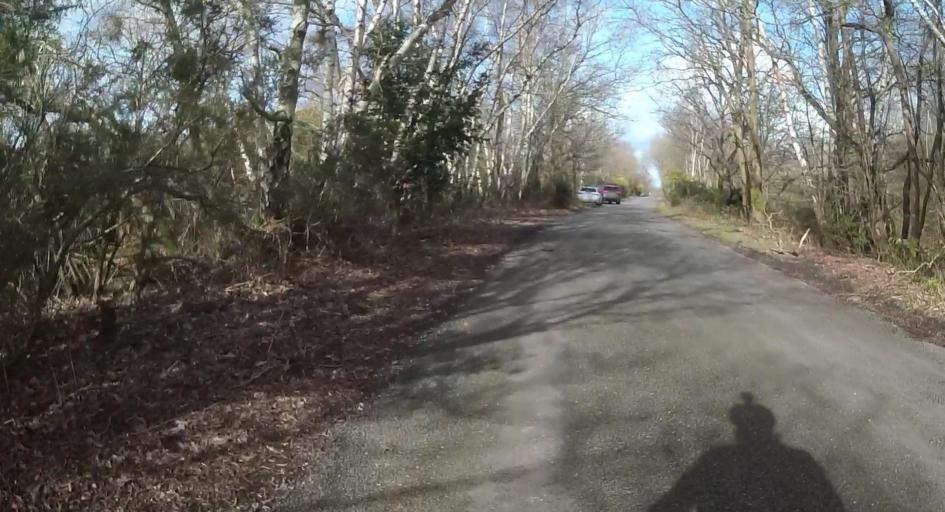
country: GB
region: England
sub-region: West Berkshire
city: Thatcham
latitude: 51.3755
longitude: -1.2554
